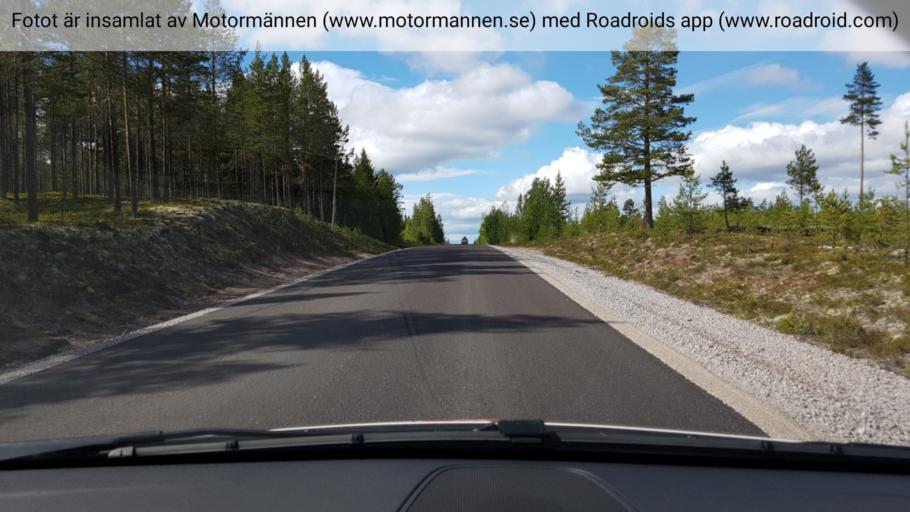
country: SE
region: Jaemtland
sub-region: Harjedalens Kommun
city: Sveg
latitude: 61.8213
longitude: 14.1014
